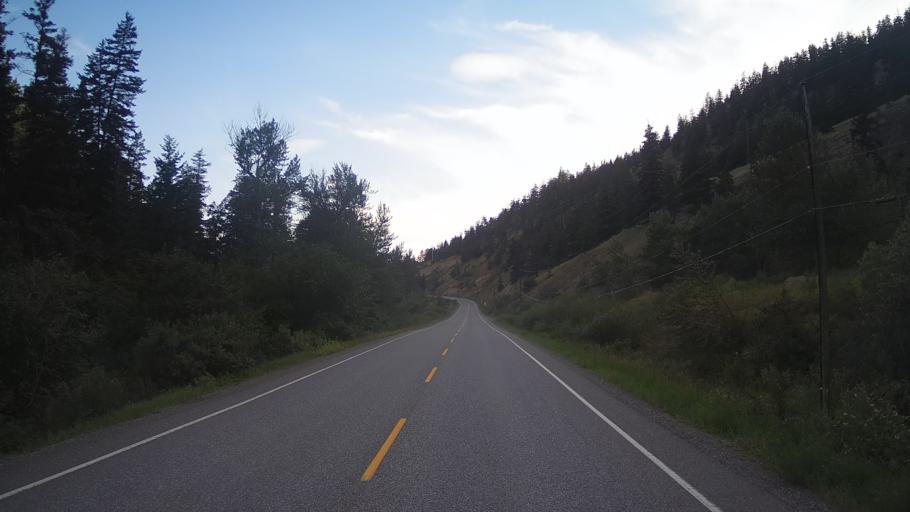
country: CA
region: British Columbia
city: Cache Creek
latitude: 50.8697
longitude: -121.5232
